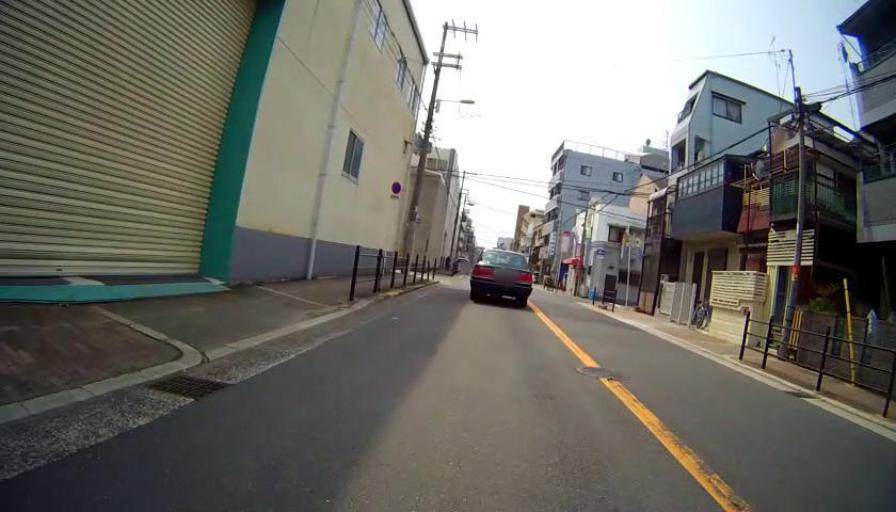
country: JP
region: Osaka
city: Suita
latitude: 34.7535
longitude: 135.5436
